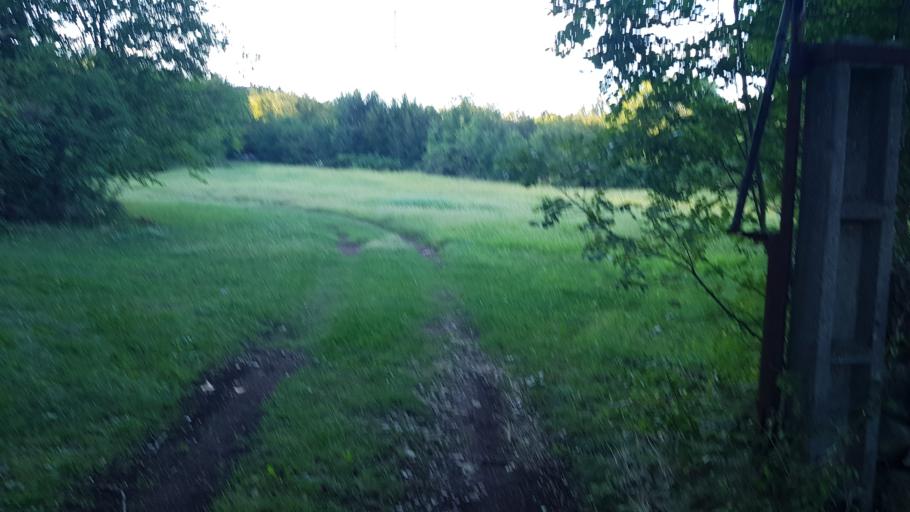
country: IT
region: Friuli Venezia Giulia
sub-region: Provincia di Trieste
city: Sistiana-Visogliano
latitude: 45.7903
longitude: 13.6375
